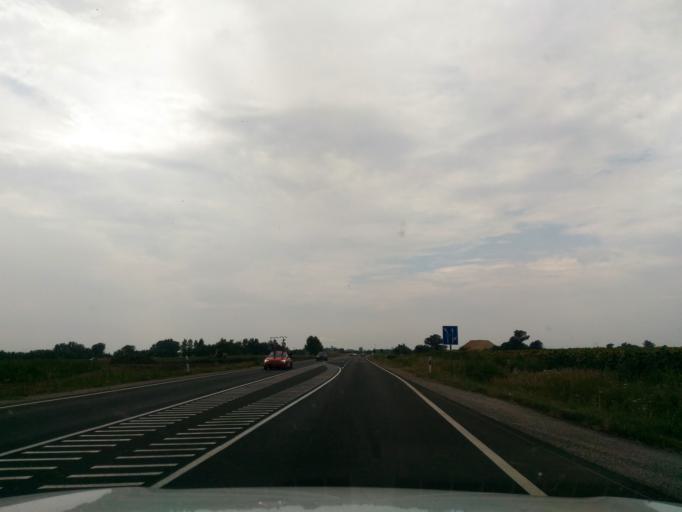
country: HU
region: Pest
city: Tortel
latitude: 47.1922
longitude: 19.9219
